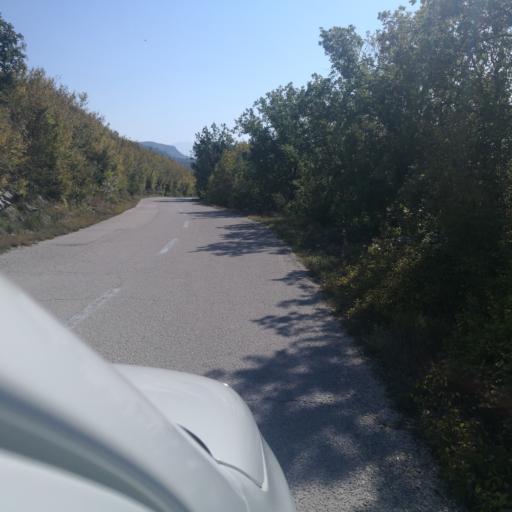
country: HR
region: Splitsko-Dalmatinska
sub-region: Grad Omis
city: Omis
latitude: 43.5219
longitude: 16.7515
